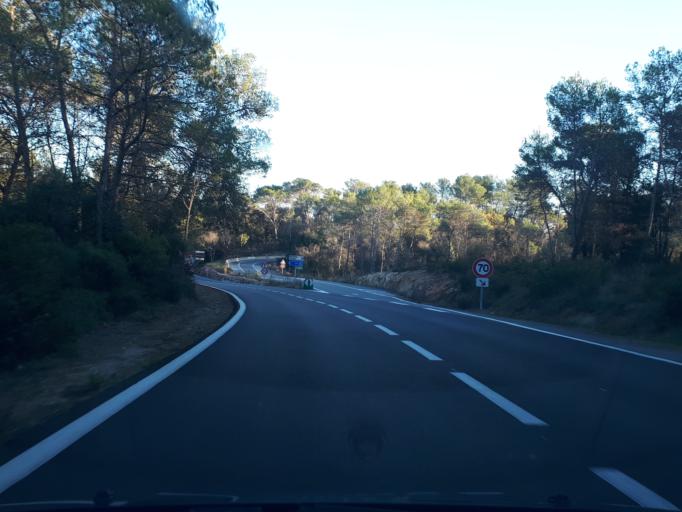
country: FR
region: Provence-Alpes-Cote d'Azur
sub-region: Departement des Alpes-Maritimes
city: Vallauris
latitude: 43.6088
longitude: 7.0525
